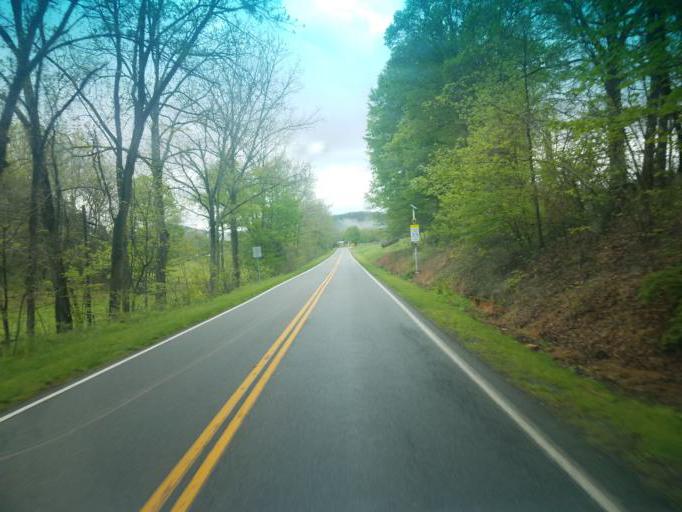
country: US
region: Virginia
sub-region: Washington County
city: Emory
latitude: 36.6555
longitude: -81.7956
